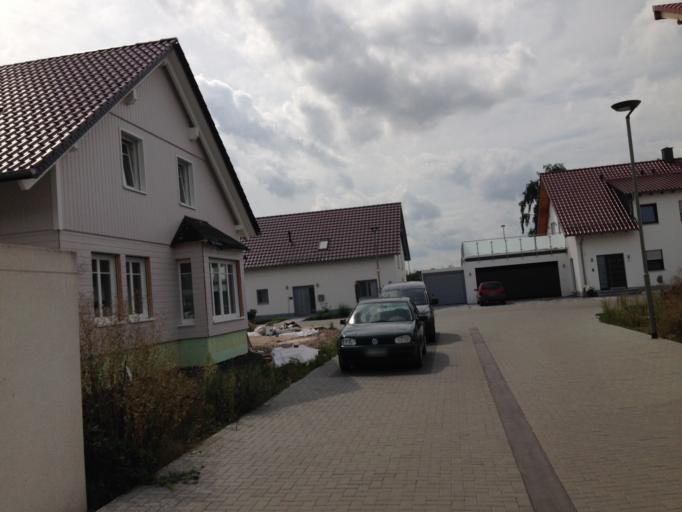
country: DE
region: Hesse
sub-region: Regierungsbezirk Giessen
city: Langgons
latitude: 50.5394
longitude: 8.6711
